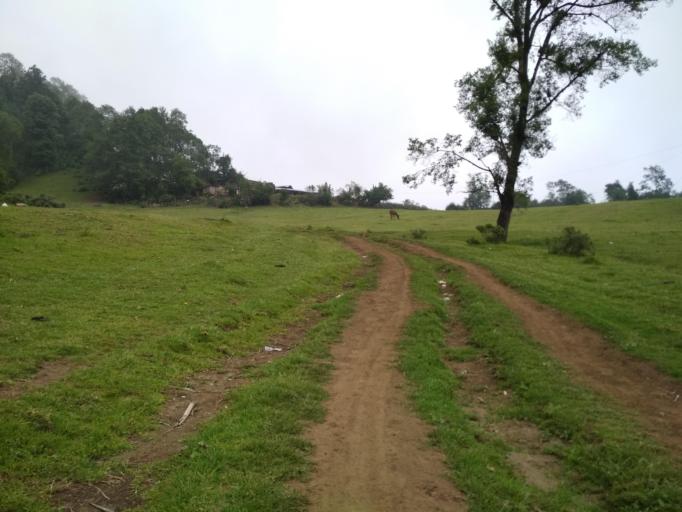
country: MX
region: Veracruz
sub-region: La Perla
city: Chilapa
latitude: 19.0007
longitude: -97.1644
